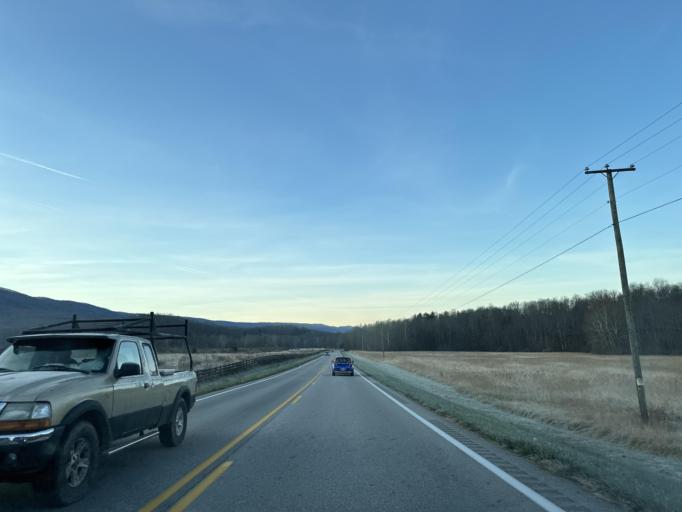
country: US
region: Virginia
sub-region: Augusta County
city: Jolivue
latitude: 38.1182
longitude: -79.2883
